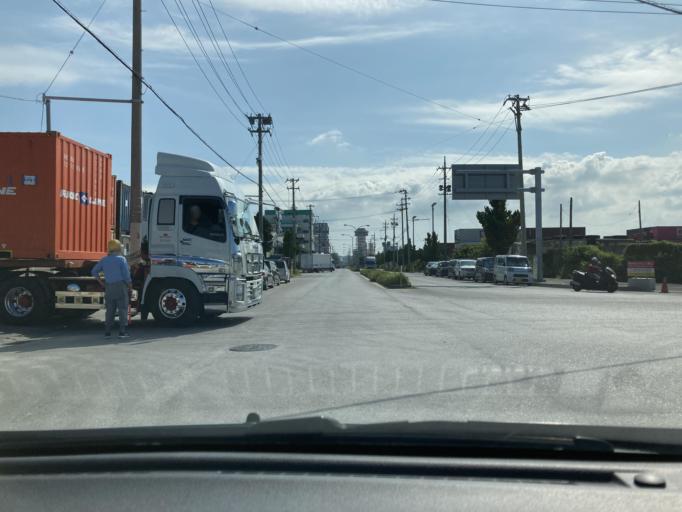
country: JP
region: Okinawa
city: Naha-shi
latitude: 26.2413
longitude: 127.6723
